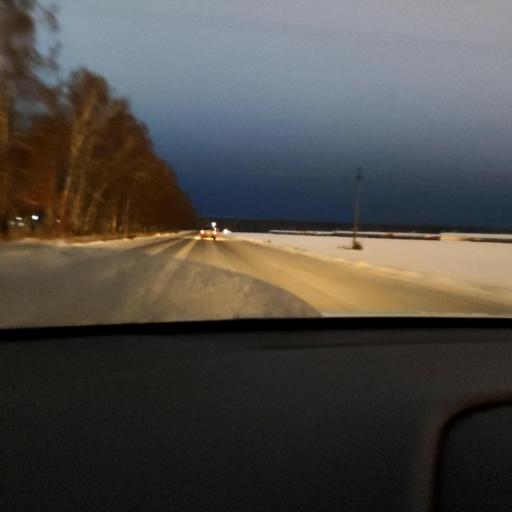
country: RU
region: Tatarstan
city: Osinovo
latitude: 55.8898
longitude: 48.8906
